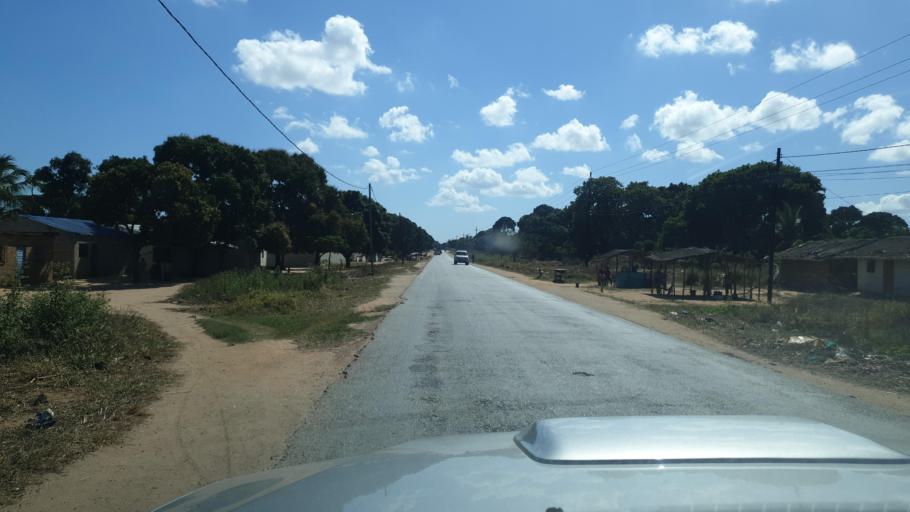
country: MZ
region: Nampula
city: Nacala
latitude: -14.5167
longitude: 40.6962
